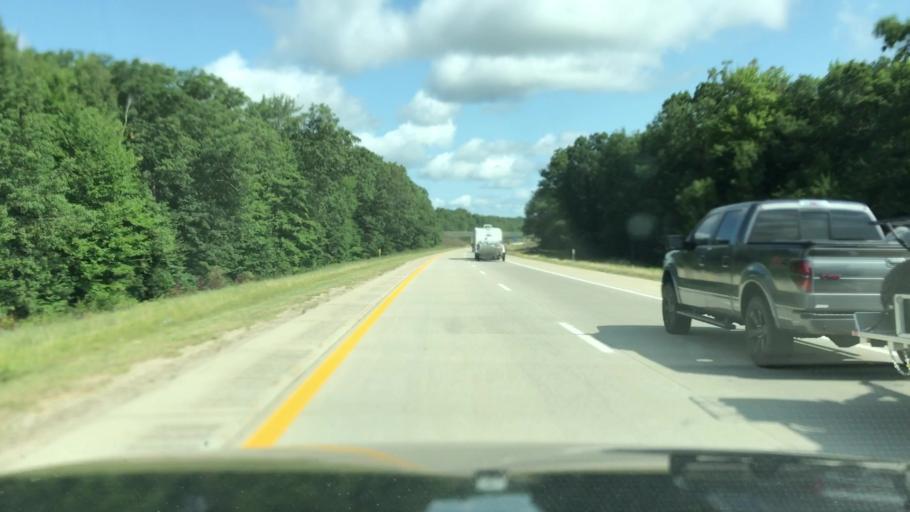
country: US
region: Michigan
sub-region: Montcalm County
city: Howard City
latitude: 43.3769
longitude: -85.5177
